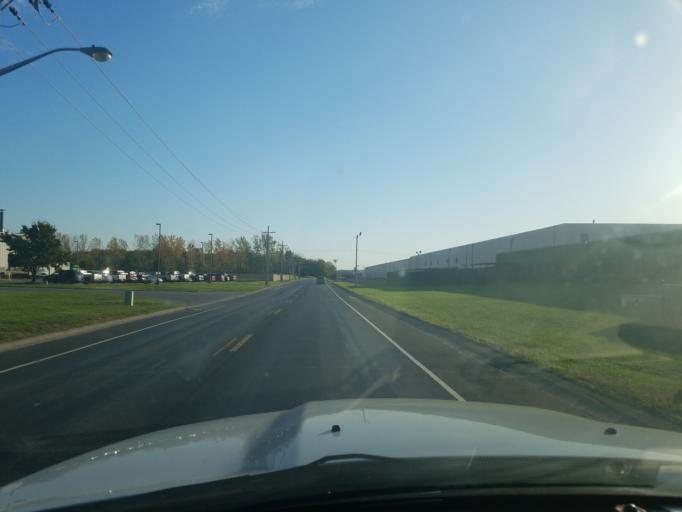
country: US
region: Indiana
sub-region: Jackson County
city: Seymour
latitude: 38.9658
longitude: -85.8687
